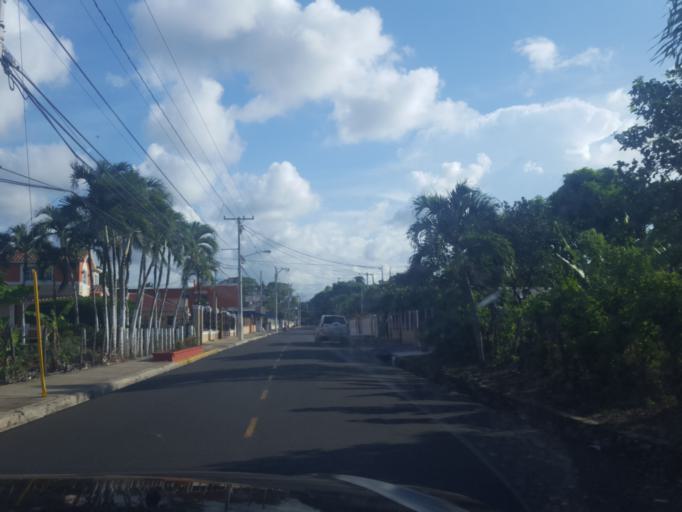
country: DO
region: Santiago
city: Licey al Medio
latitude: 19.3832
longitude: -70.6317
